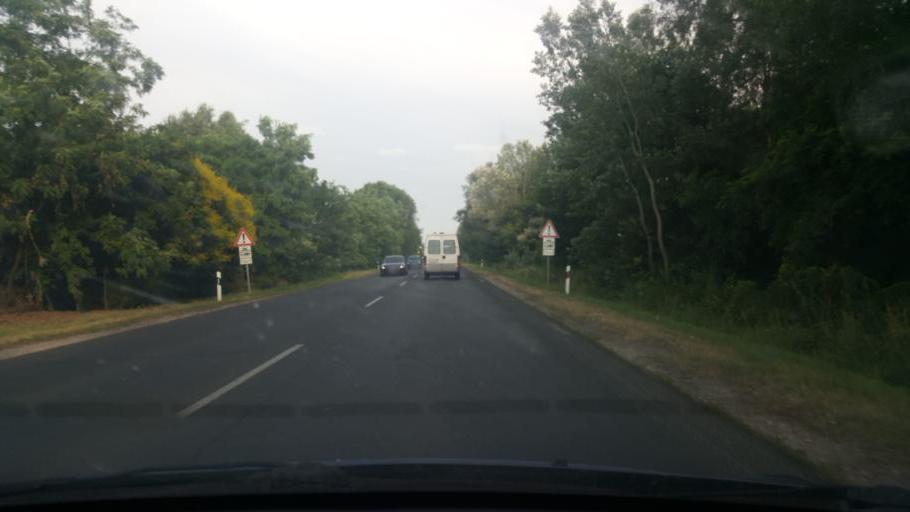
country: HU
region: Pest
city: Monor
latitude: 47.3397
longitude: 19.4301
